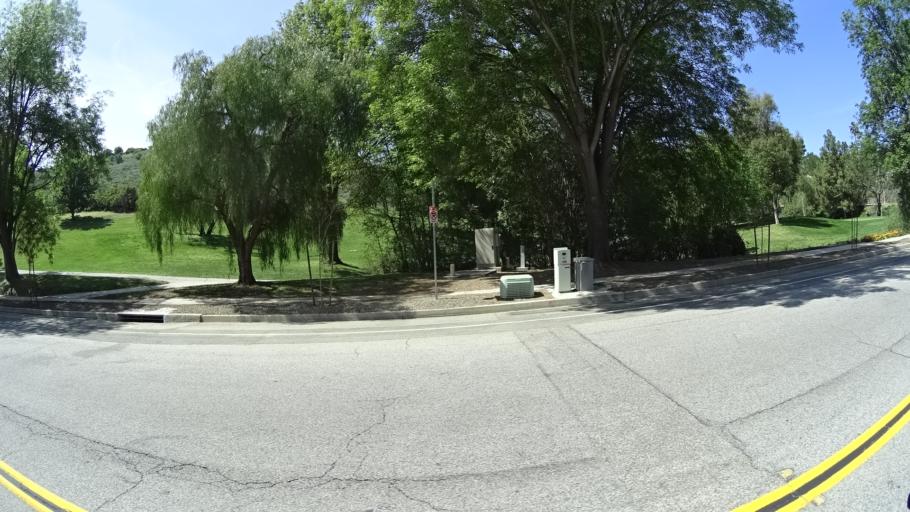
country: US
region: California
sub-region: Ventura County
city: Moorpark
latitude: 34.2379
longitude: -118.8476
